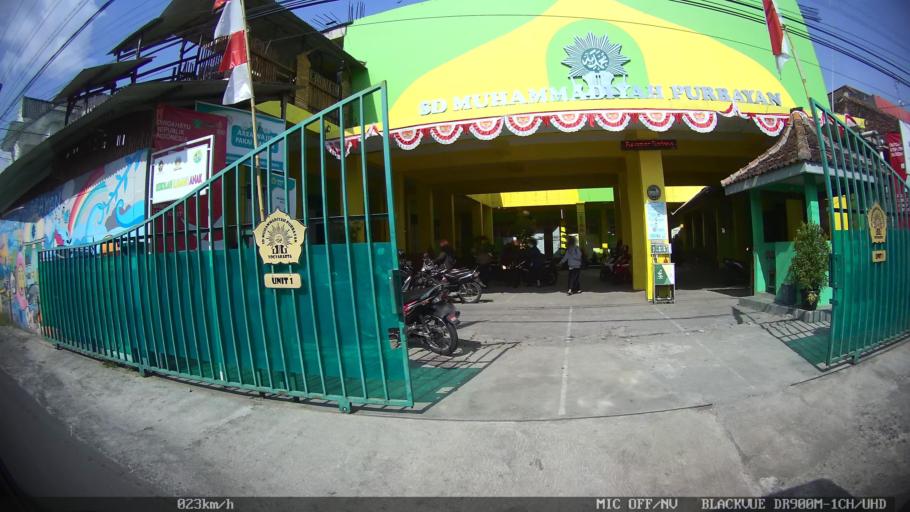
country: ID
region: Daerah Istimewa Yogyakarta
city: Yogyakarta
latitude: -7.8291
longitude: 110.4027
